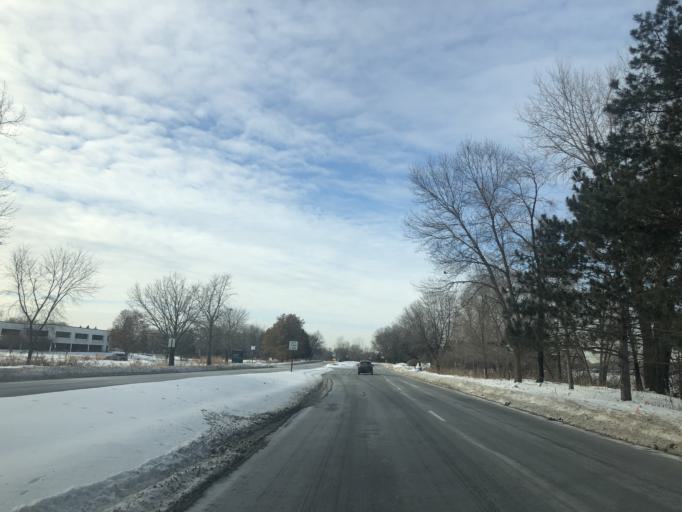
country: US
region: Minnesota
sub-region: Anoka County
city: Circle Pines
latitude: 45.1624
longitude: -93.1656
